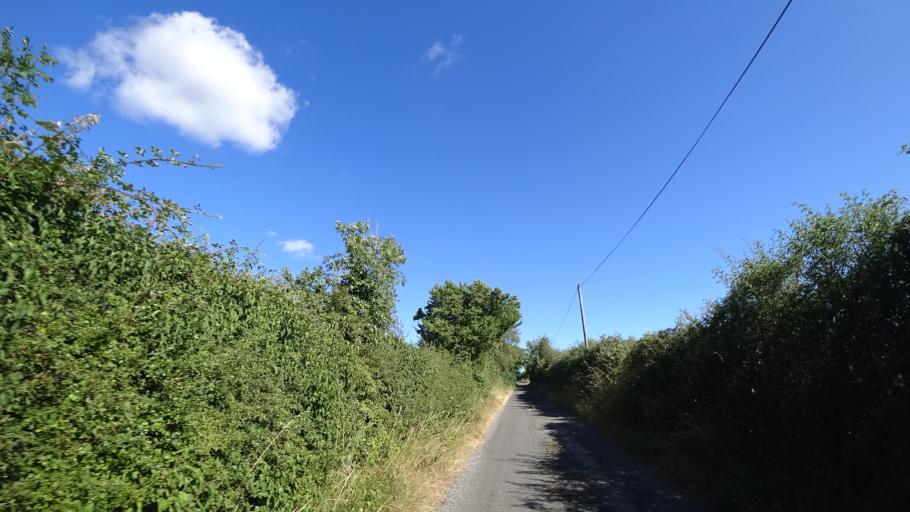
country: FR
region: Midi-Pyrenees
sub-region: Departement de l'Aveyron
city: Druelle
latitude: 44.3867
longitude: 2.5043
